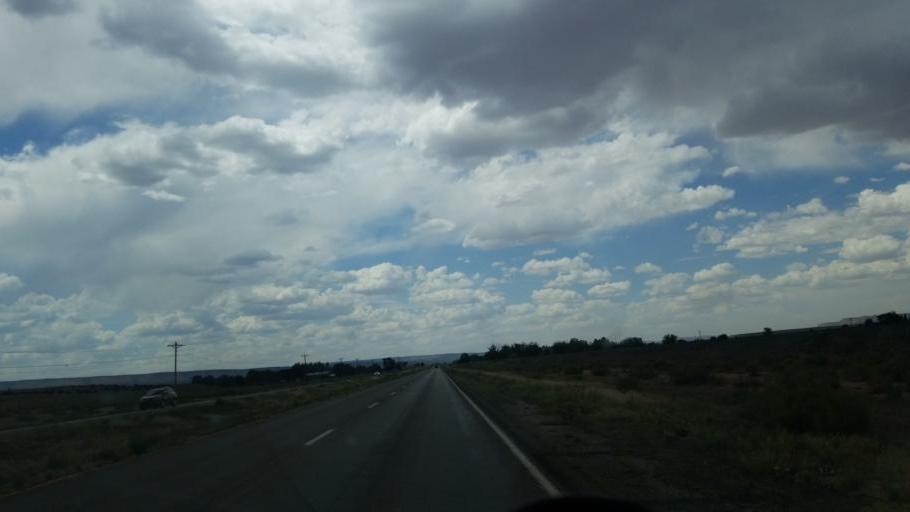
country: US
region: New Mexico
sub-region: Cibola County
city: Milan
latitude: 35.2282
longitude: -107.9257
